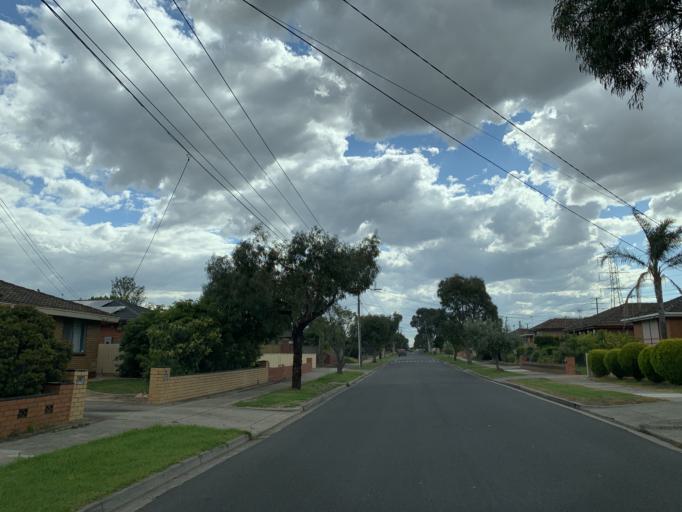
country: AU
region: Victoria
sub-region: Moonee Valley
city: Keilor East
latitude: -37.7414
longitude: 144.8594
